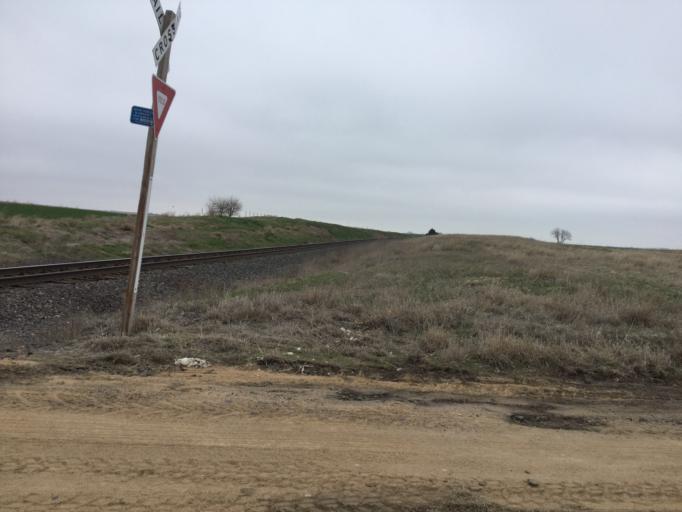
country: US
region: Kansas
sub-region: Russell County
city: Russell
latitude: 38.8414
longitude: -98.5581
